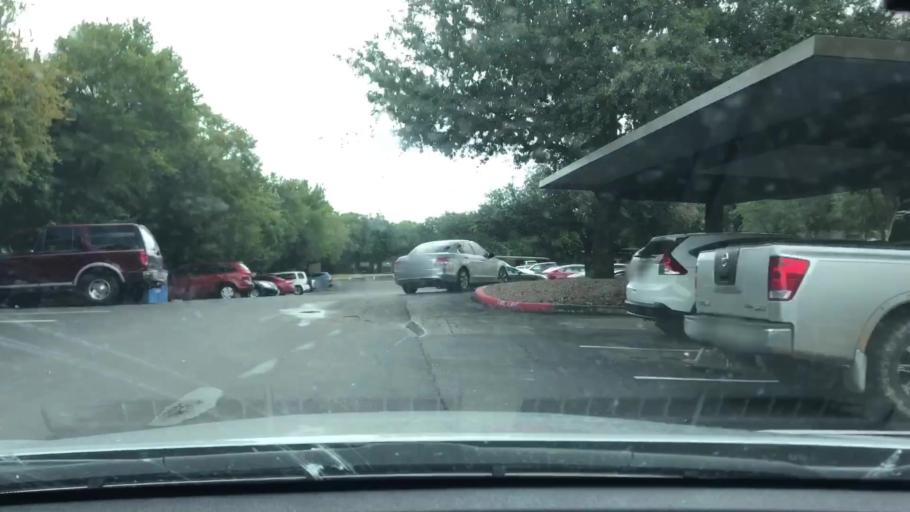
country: US
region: Texas
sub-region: Bexar County
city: Balcones Heights
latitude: 29.5154
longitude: -98.5618
